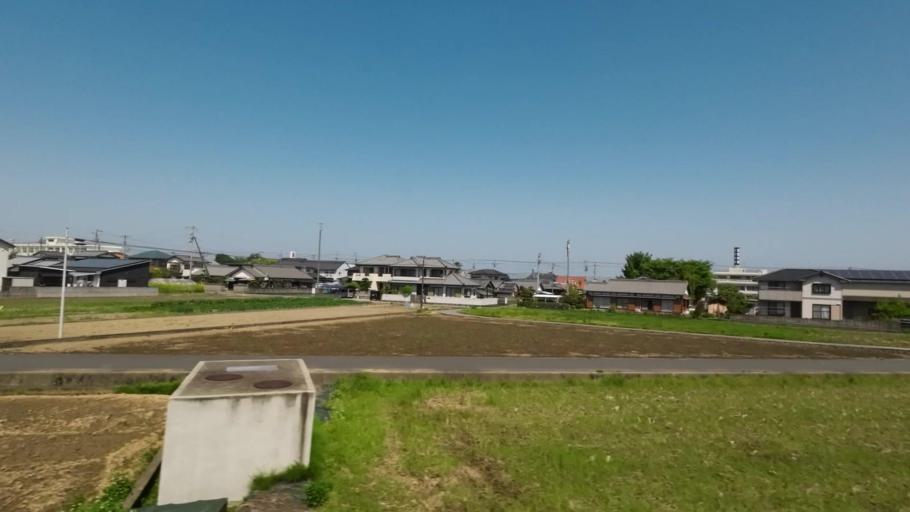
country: JP
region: Ehime
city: Niihama
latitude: 33.9673
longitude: 133.3188
